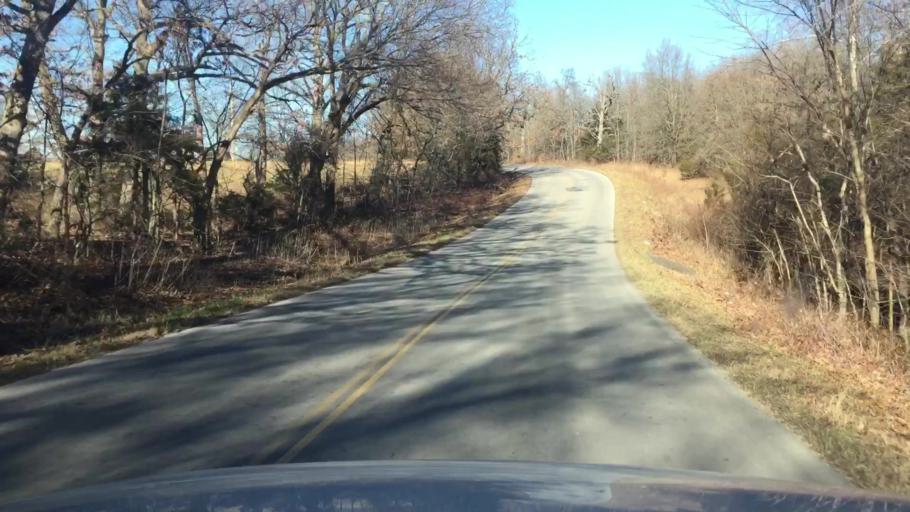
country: US
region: Missouri
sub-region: Morgan County
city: Versailles
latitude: 38.3436
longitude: -92.7493
